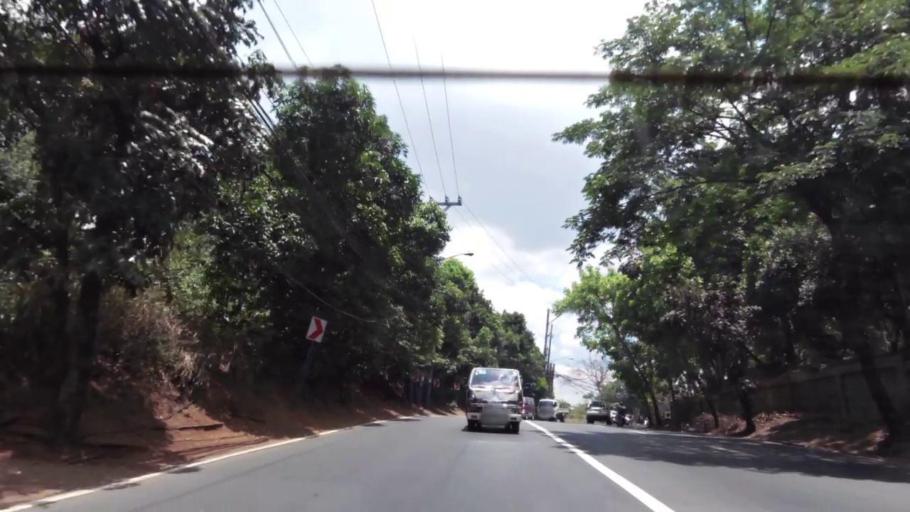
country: PH
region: Calabarzon
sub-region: Province of Rizal
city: Cainta
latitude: 14.5992
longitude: 121.1732
